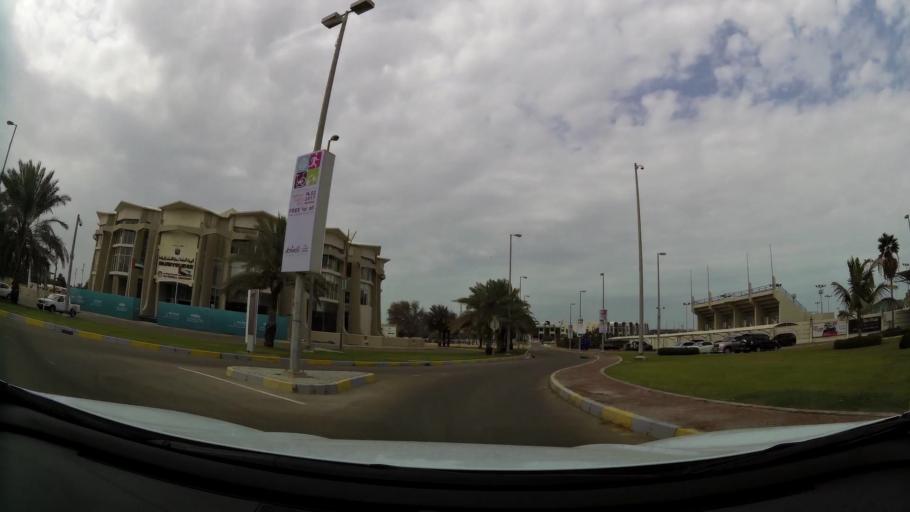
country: AE
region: Abu Dhabi
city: Abu Dhabi
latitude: 24.4129
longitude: 54.4586
